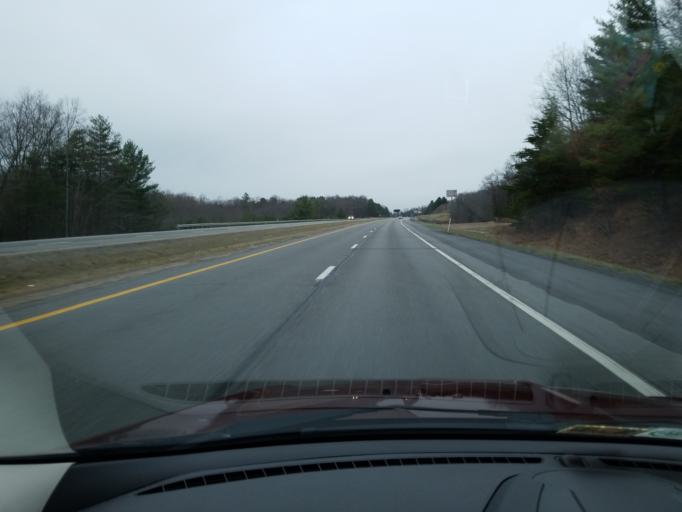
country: US
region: West Virginia
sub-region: Mercer County
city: Athens
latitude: 37.3574
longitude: -81.0237
